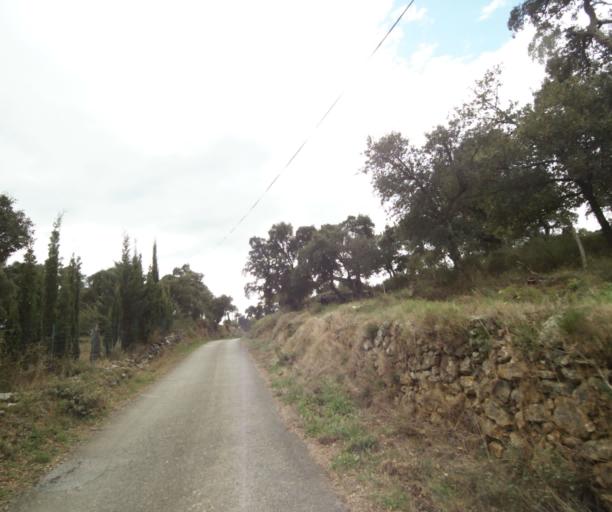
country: FR
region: Languedoc-Roussillon
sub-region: Departement des Pyrenees-Orientales
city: Collioure
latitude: 42.5221
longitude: 3.0513
